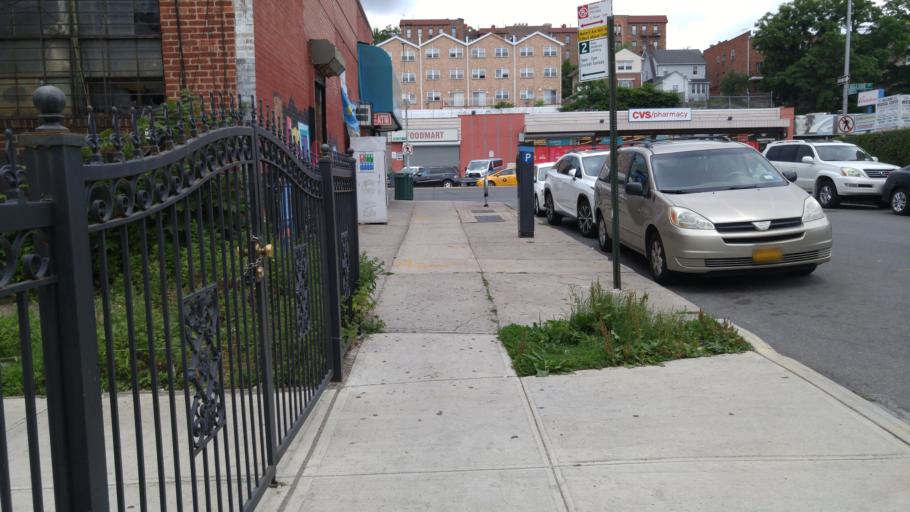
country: US
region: New York
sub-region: Queens County
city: Jamaica
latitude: 40.7111
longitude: -73.7908
